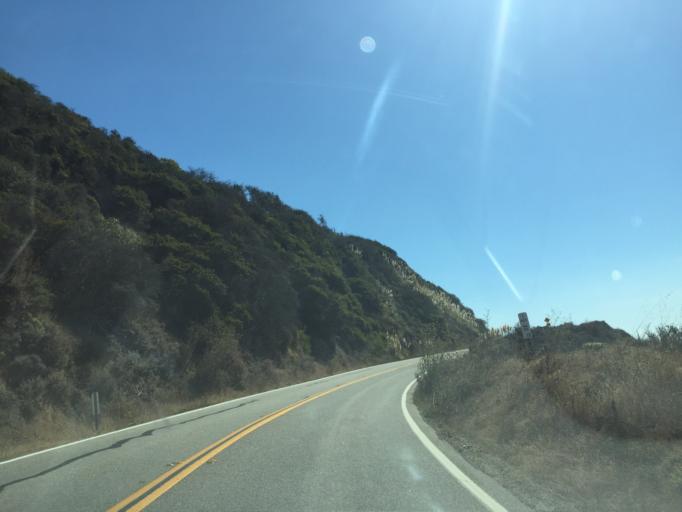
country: US
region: California
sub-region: Monterey County
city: Greenfield
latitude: 36.0903
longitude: -121.6176
